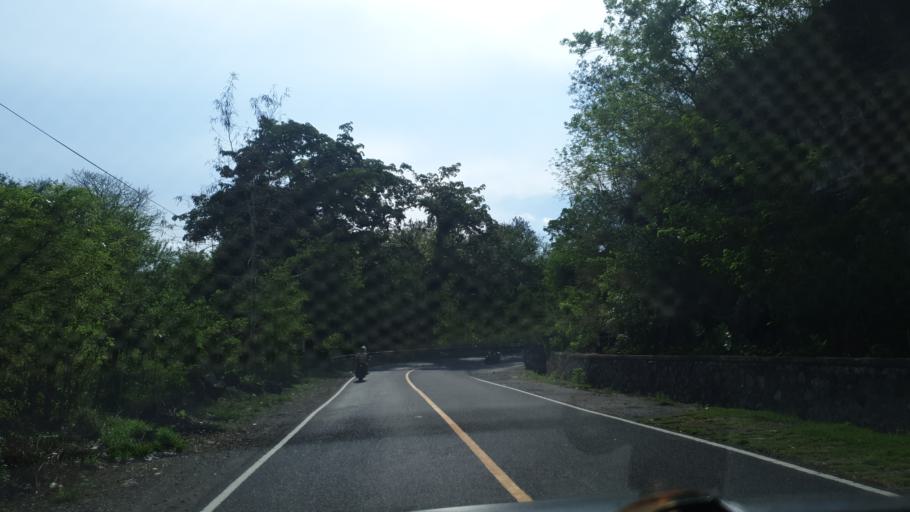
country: ID
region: East Nusa Tenggara
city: Nangalimang
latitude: -8.6604
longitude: 122.2009
